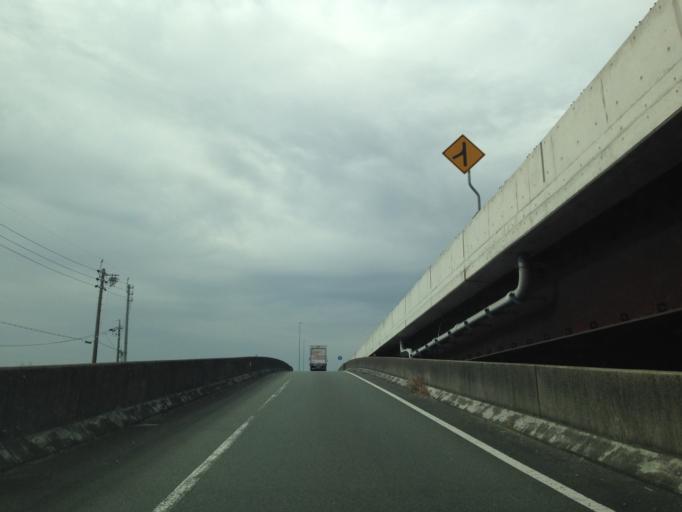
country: JP
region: Shizuoka
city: Fukuroi
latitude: 34.7514
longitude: 137.9046
